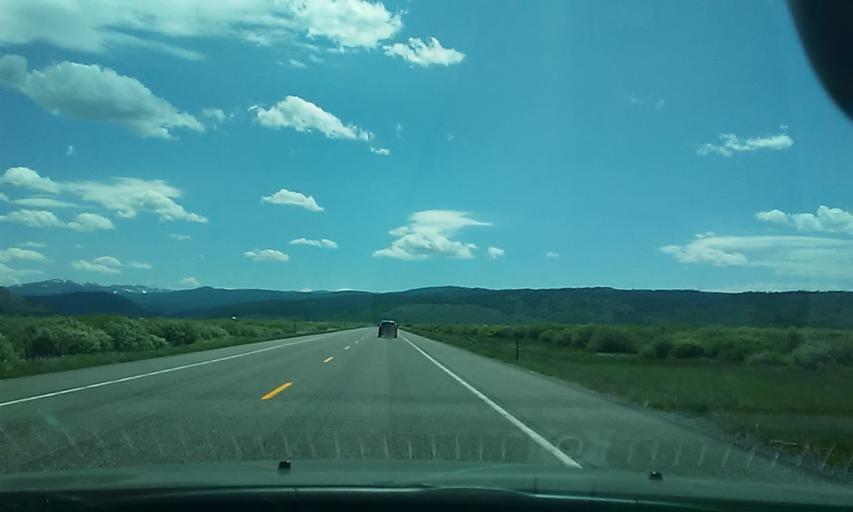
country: US
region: Wyoming
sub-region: Teton County
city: Jackson
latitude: 43.8360
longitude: -110.4328
